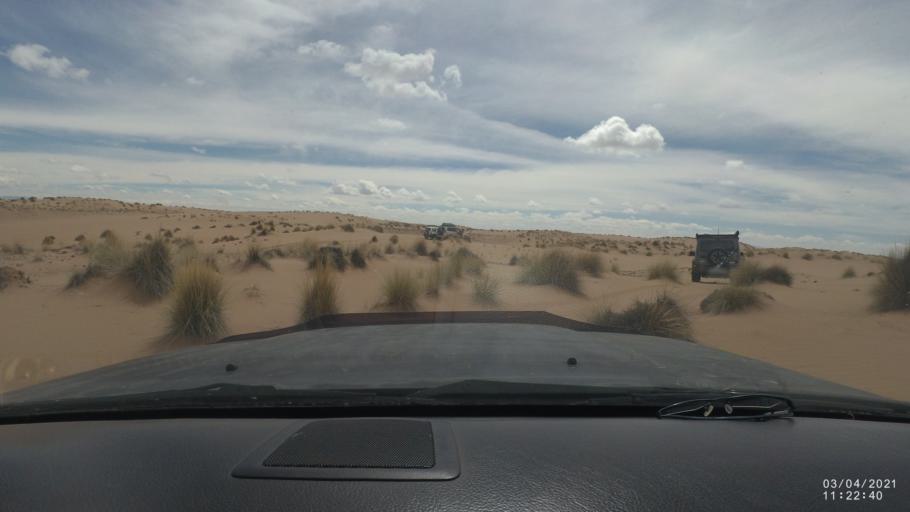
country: BO
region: Oruro
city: Poopo
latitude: -18.7032
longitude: -67.5116
